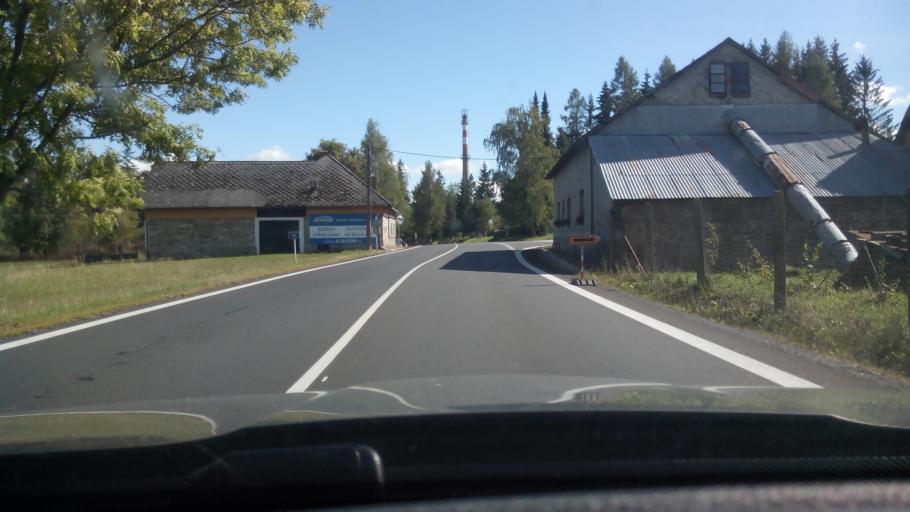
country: CZ
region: Jihocesky
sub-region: Okres Prachatice
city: Zdikov
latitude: 49.0635
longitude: 13.7366
